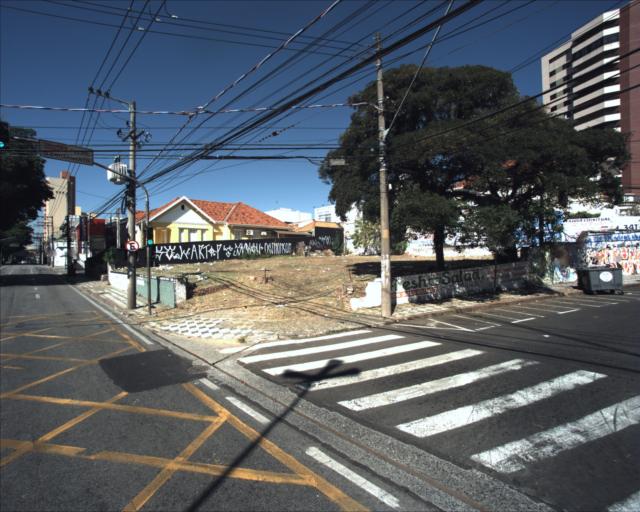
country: BR
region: Sao Paulo
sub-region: Sorocaba
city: Sorocaba
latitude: -23.5036
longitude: -47.4666
